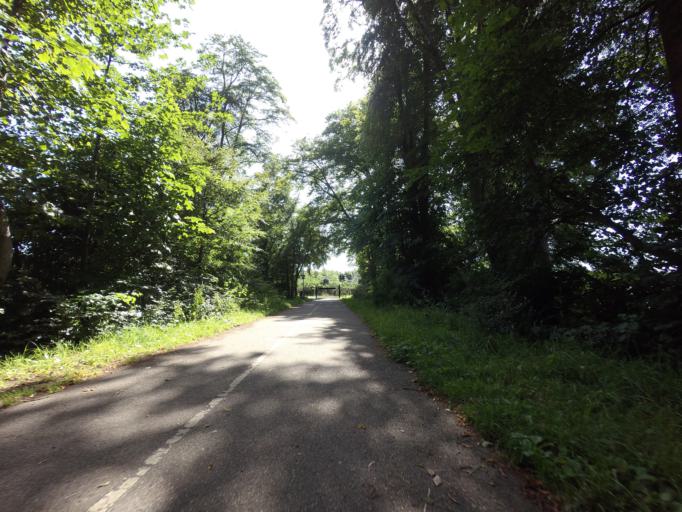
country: GB
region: Scotland
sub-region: Highland
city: Inverness
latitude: 57.4847
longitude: -4.1428
